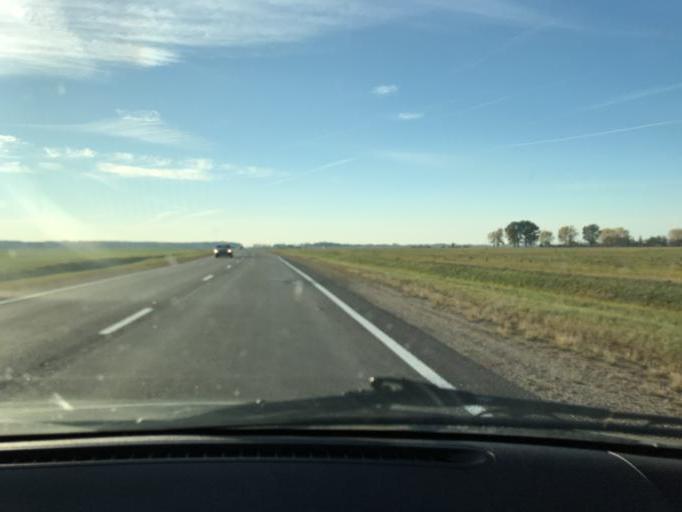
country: BY
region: Brest
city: Antopal'
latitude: 52.2280
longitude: 24.8004
